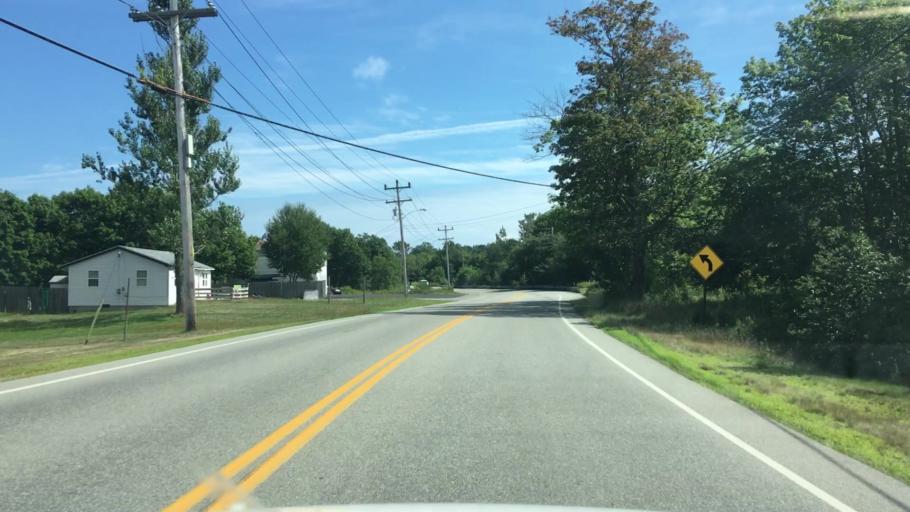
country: US
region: Maine
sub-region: Washington County
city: Eastport
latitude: 44.9149
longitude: -67.0073
